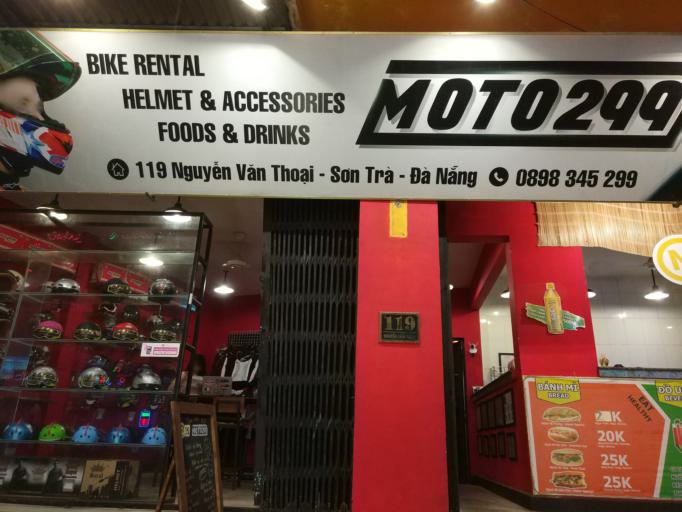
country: VN
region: Da Nang
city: Son Tra
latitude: 16.0545
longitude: 108.2400
